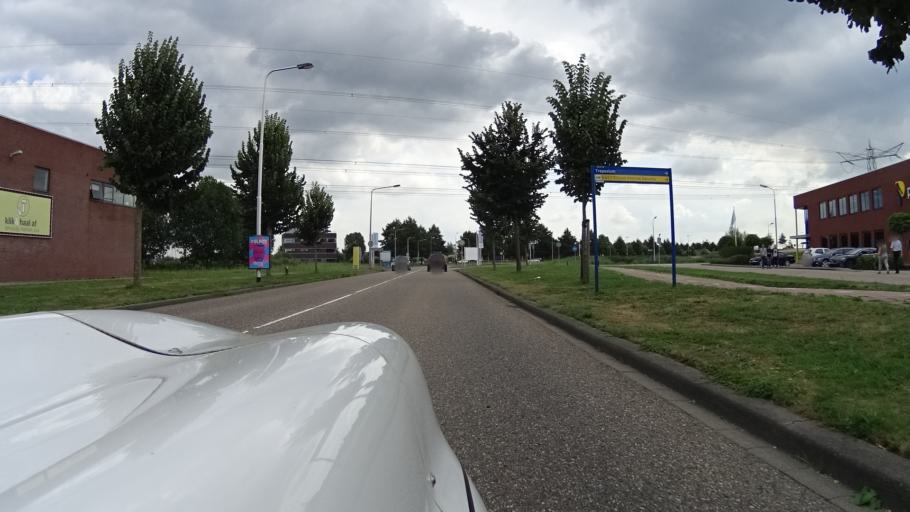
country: NL
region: South Holland
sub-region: Gemeente Sliedrecht
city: Sliedrecht
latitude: 51.8264
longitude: 4.8025
